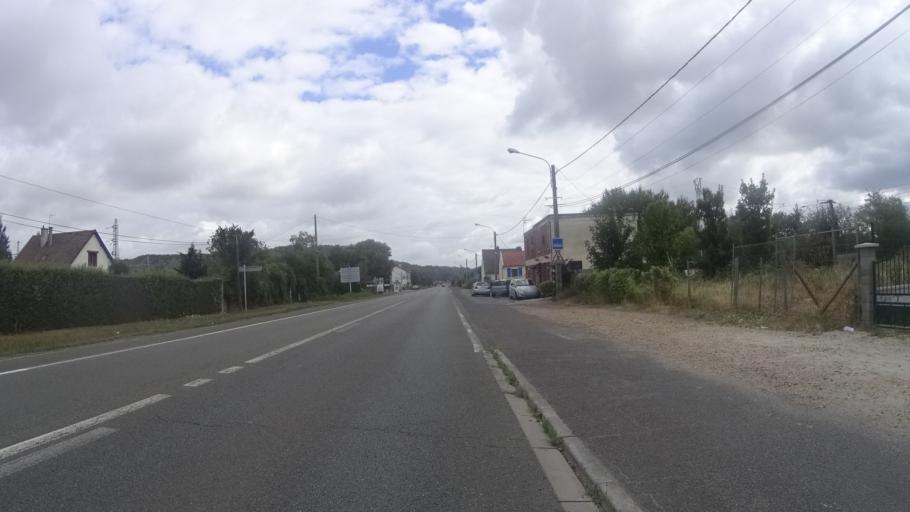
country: FR
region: Picardie
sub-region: Departement de l'Oise
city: Clairoix
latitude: 49.4332
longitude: 2.8409
